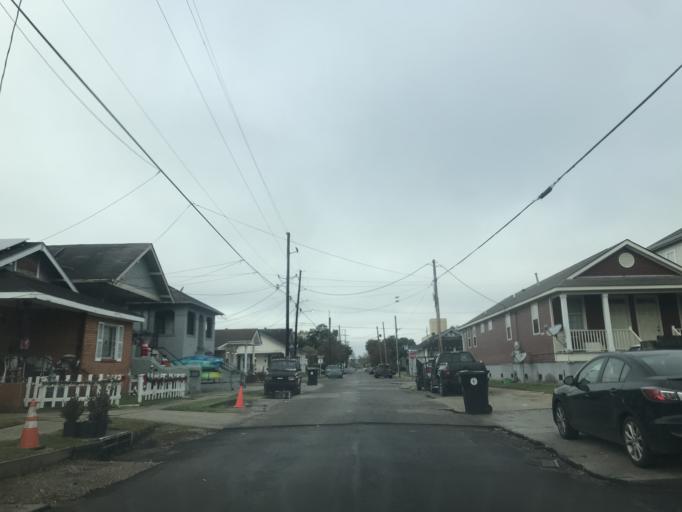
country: US
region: Louisiana
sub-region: Orleans Parish
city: New Orleans
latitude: 29.9716
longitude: -90.1066
